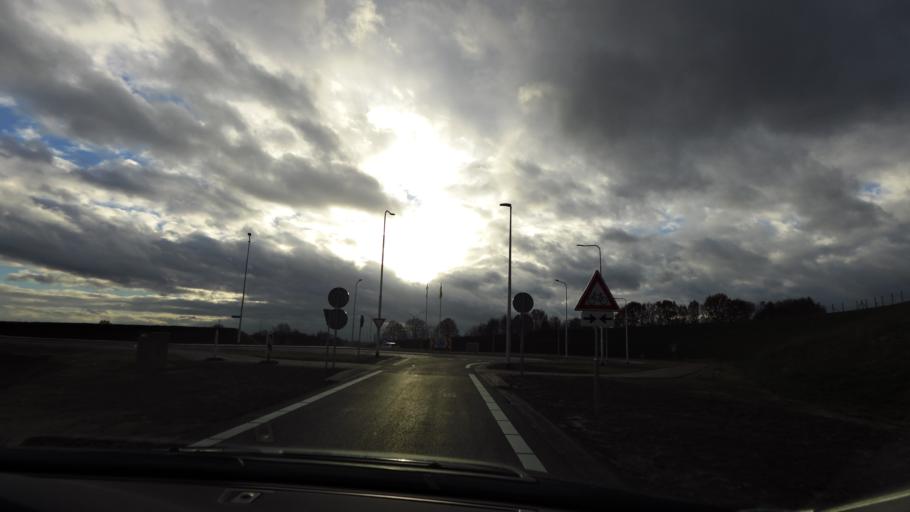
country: NL
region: Limburg
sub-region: Gemeente Kerkrade
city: Kerkrade
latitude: 50.8559
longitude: 6.0439
